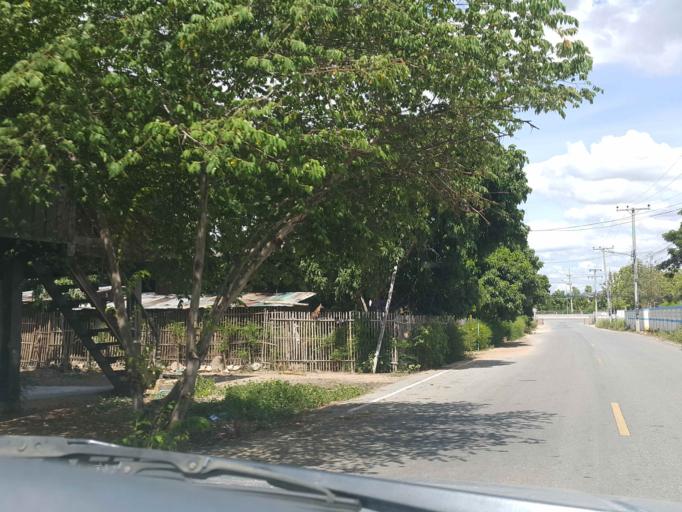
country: TH
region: Chiang Mai
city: Doi Lo
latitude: 18.4559
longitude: 98.7692
